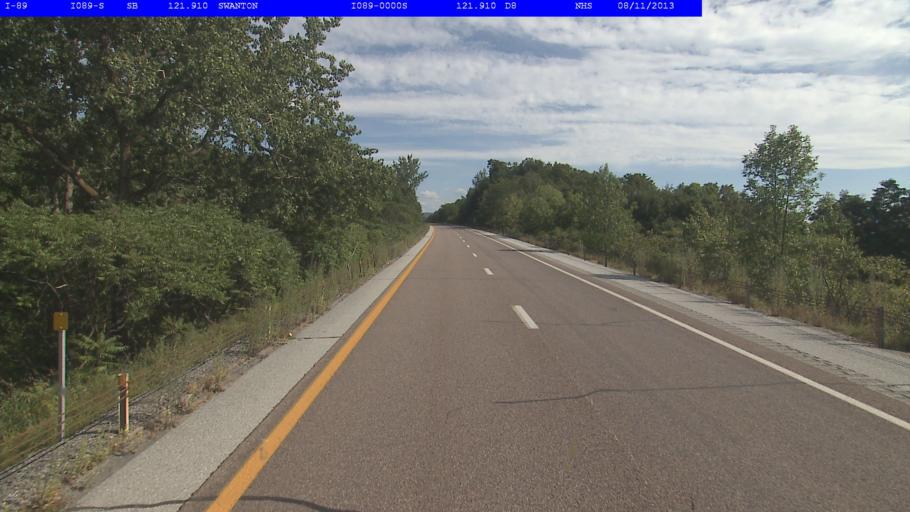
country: US
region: Vermont
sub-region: Franklin County
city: Swanton
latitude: 44.9028
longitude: -73.0962
